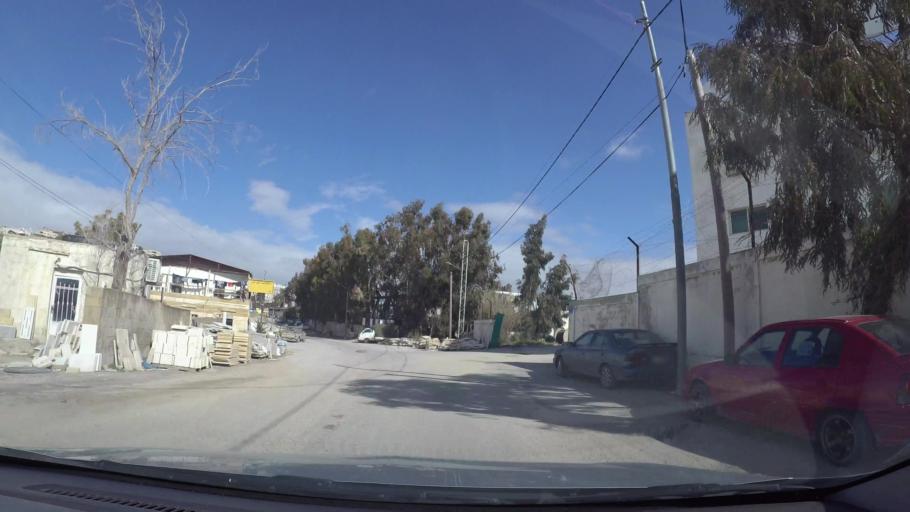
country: JO
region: Amman
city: Al Jubayhah
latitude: 32.0137
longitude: 35.8447
